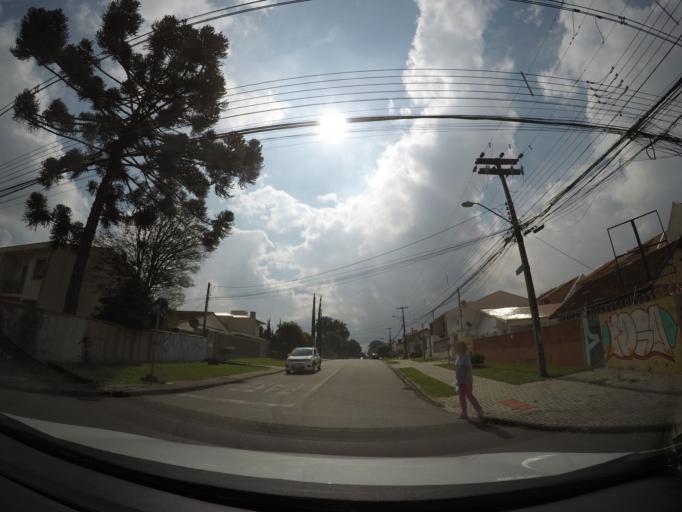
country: BR
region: Parana
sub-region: Curitiba
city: Curitiba
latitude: -25.4842
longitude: -49.2500
